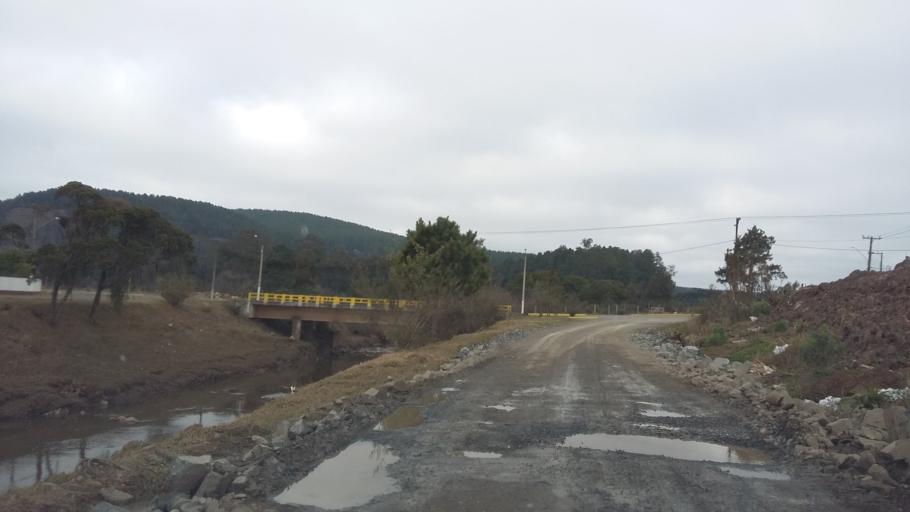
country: BR
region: Santa Catarina
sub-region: Lages
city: Lages
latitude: -27.8379
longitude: -50.3226
